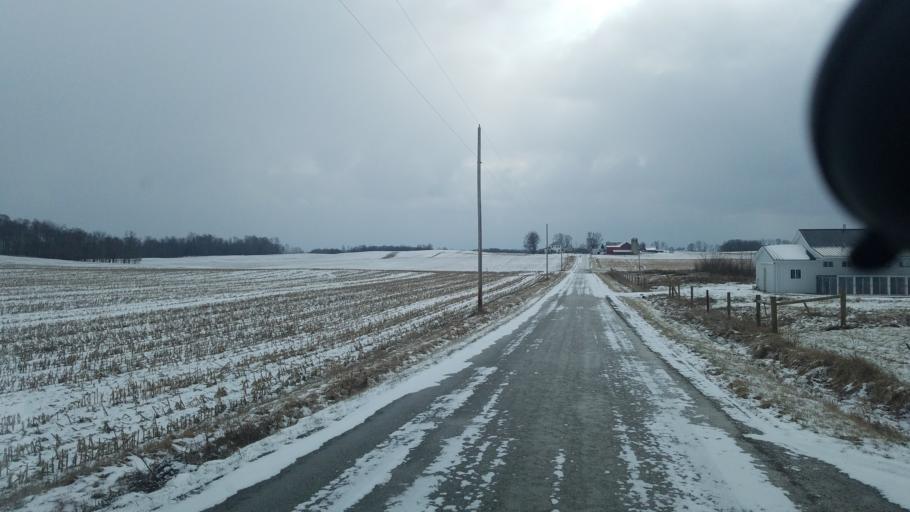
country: US
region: Ohio
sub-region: Morrow County
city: Mount Gilead
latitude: 40.5455
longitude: -82.7204
